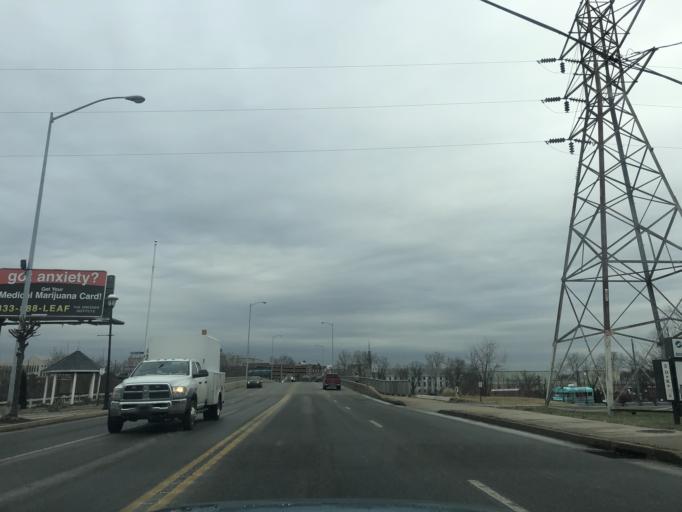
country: US
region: Pennsylvania
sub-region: Montgomery County
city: Bridgeport
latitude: 40.1084
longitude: -75.3451
